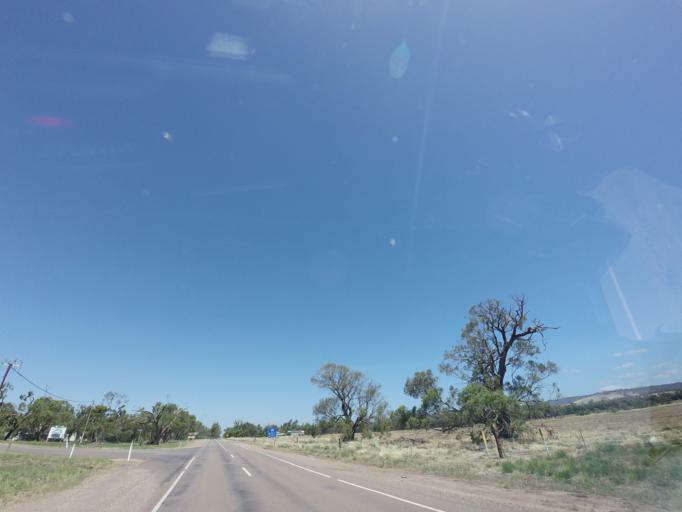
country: AU
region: South Australia
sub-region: Flinders Ranges
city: Quorn
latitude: -32.6604
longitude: 138.1067
